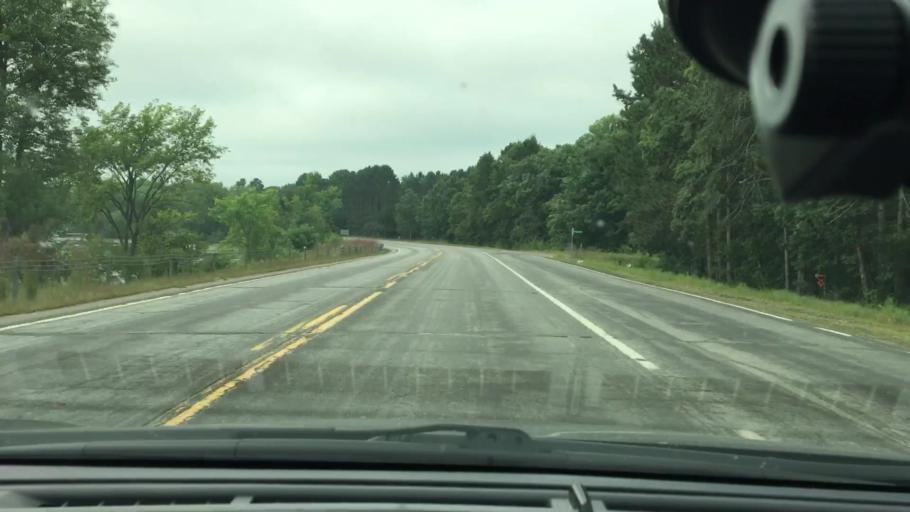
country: US
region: Minnesota
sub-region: Crow Wing County
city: Cross Lake
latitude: 46.7257
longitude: -93.9584
